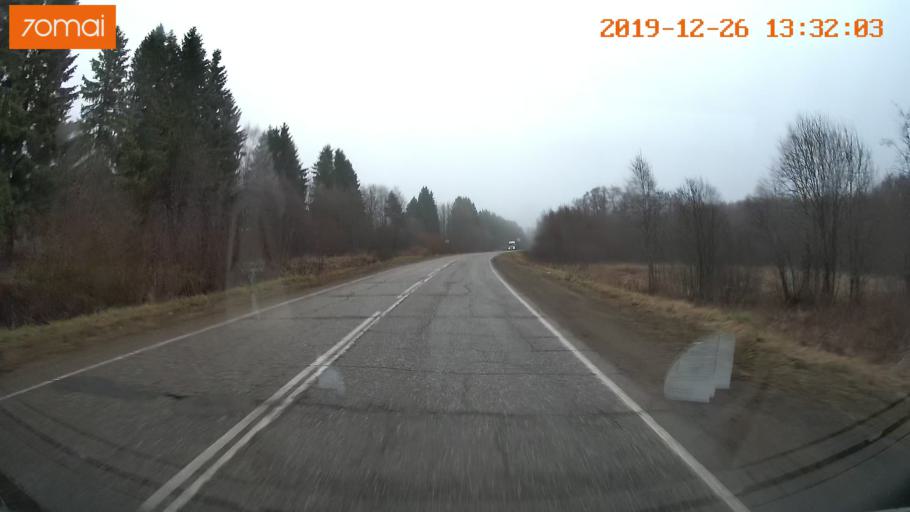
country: RU
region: Vologda
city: Sheksna
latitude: 58.8326
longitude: 38.2828
